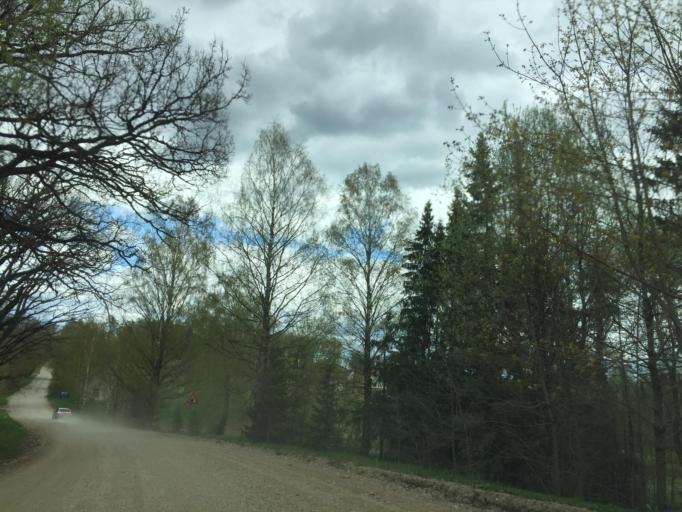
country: LV
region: Madonas Rajons
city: Madona
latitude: 56.9227
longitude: 26.0491
